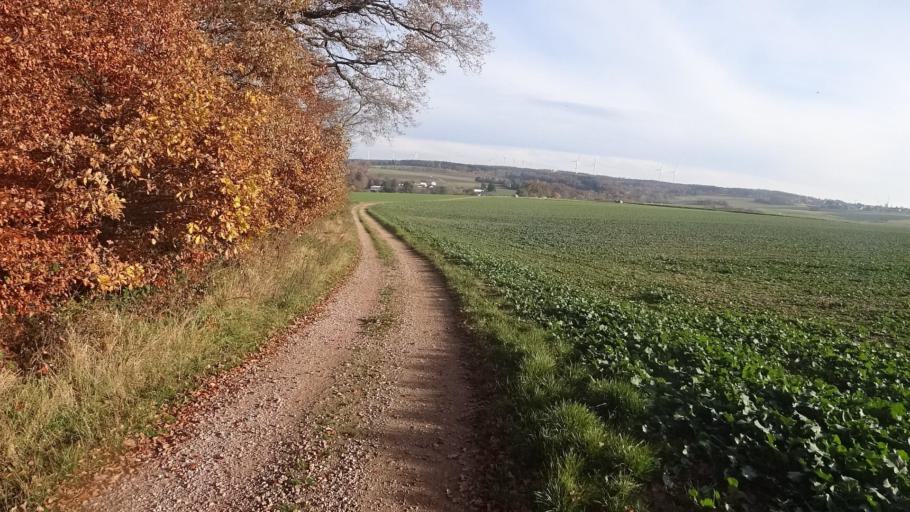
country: DE
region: Rheinland-Pfalz
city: Hausbay
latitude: 50.1101
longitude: 7.5503
